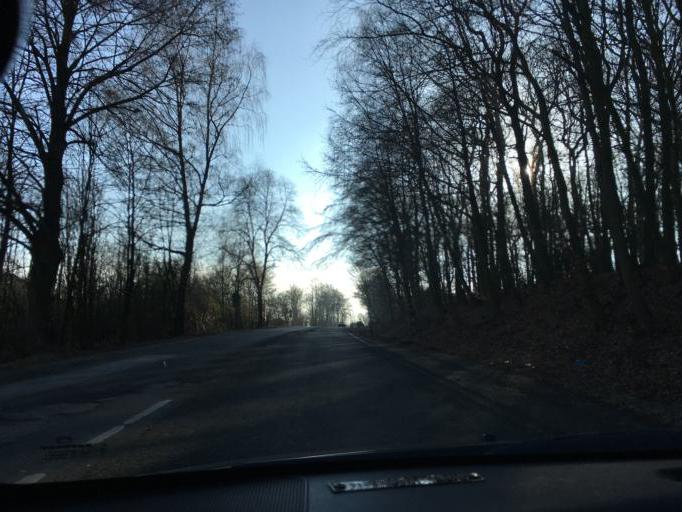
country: DE
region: North Rhine-Westphalia
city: Schwerte
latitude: 51.4301
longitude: 7.6187
